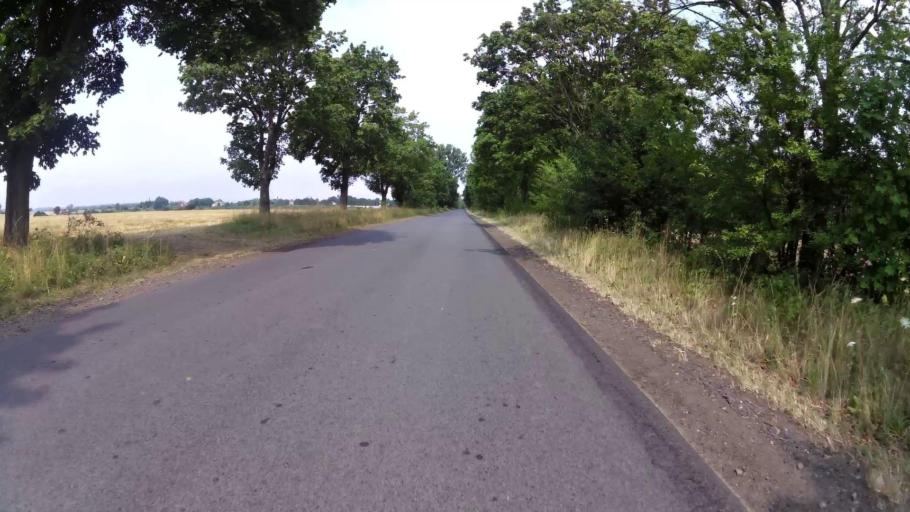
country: PL
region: West Pomeranian Voivodeship
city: Trzcinsko Zdroj
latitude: 52.9580
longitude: 14.6219
